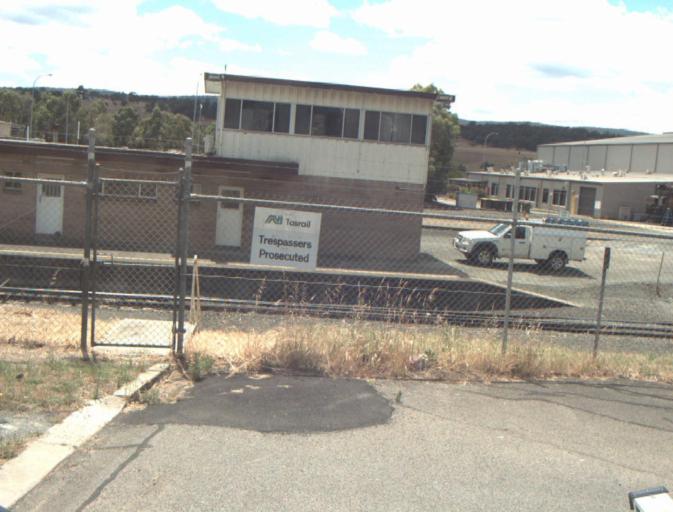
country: AU
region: Tasmania
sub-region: Launceston
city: Newstead
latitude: -41.4309
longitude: 147.1600
